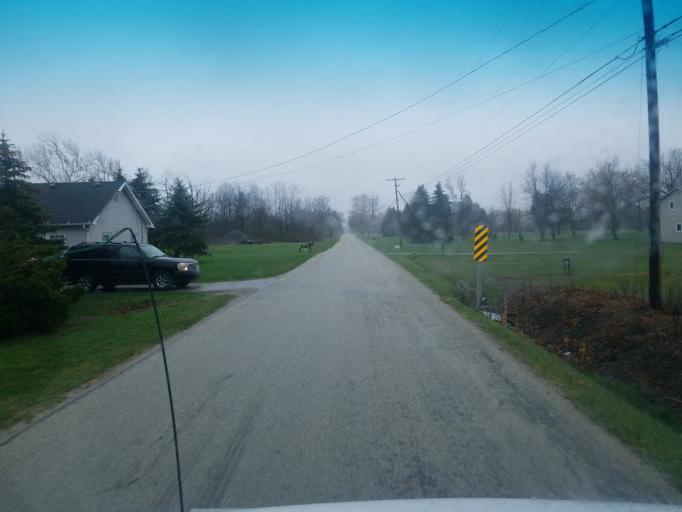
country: US
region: Ohio
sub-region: Wood County
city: North Baltimore
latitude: 41.2466
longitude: -83.6308
